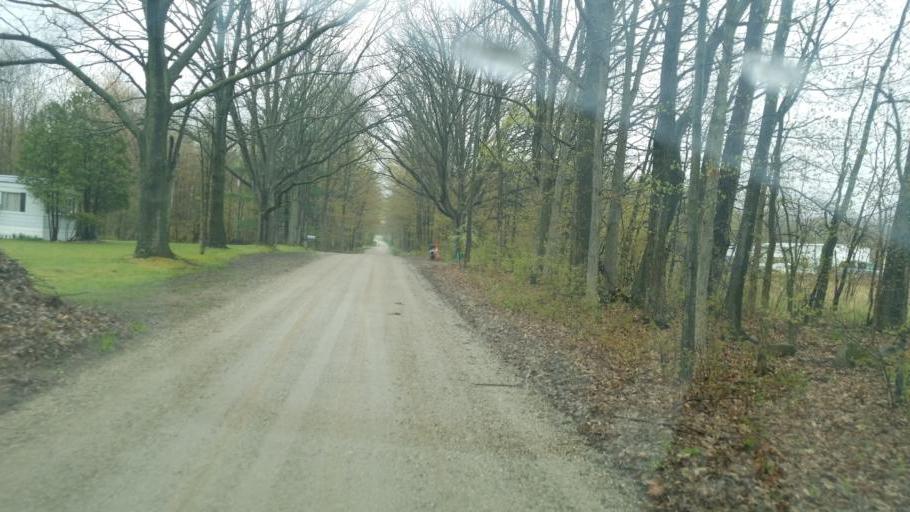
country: US
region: Michigan
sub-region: Mecosta County
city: Canadian Lakes
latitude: 43.5043
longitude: -85.3305
